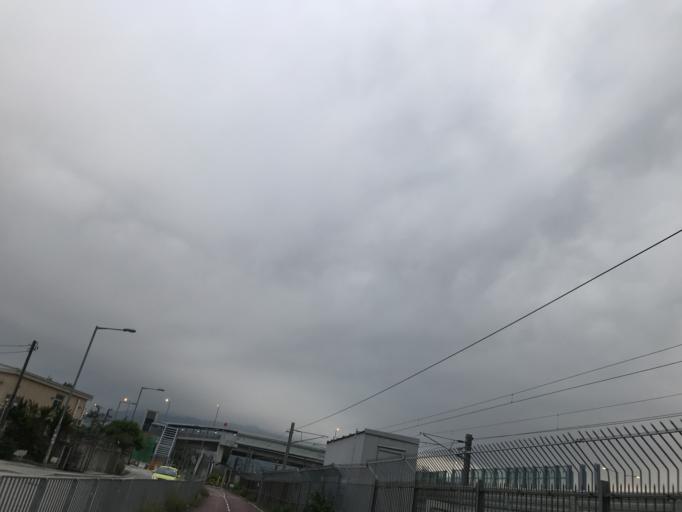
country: HK
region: Tai Po
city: Tai Po
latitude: 22.4765
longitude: 114.1547
